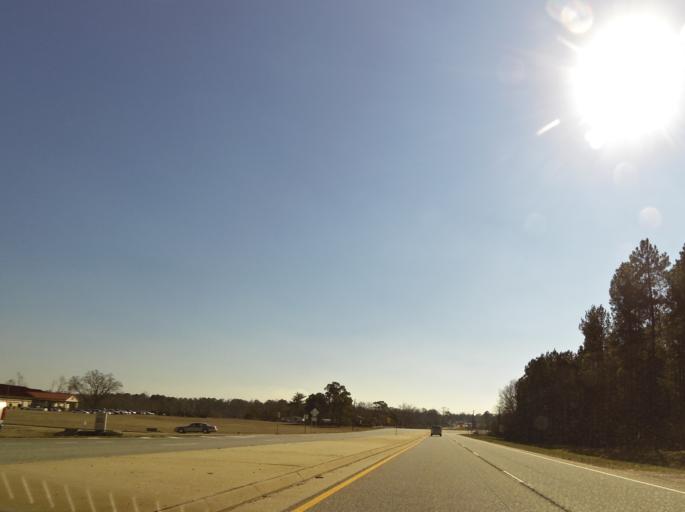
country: US
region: Georgia
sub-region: Pulaski County
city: Hawkinsville
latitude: 32.2953
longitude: -83.4859
